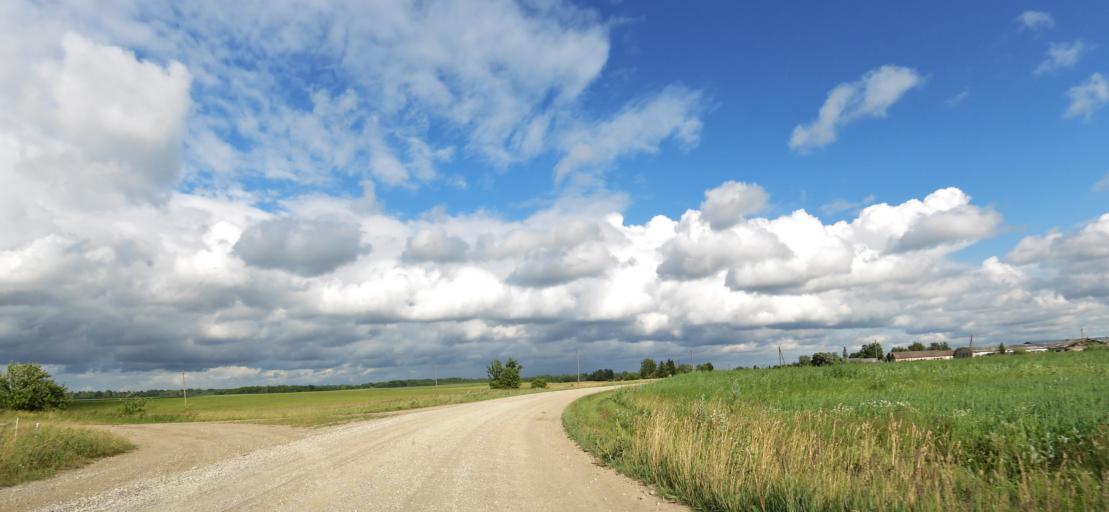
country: LT
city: Obeliai
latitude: 55.9088
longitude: 25.1133
